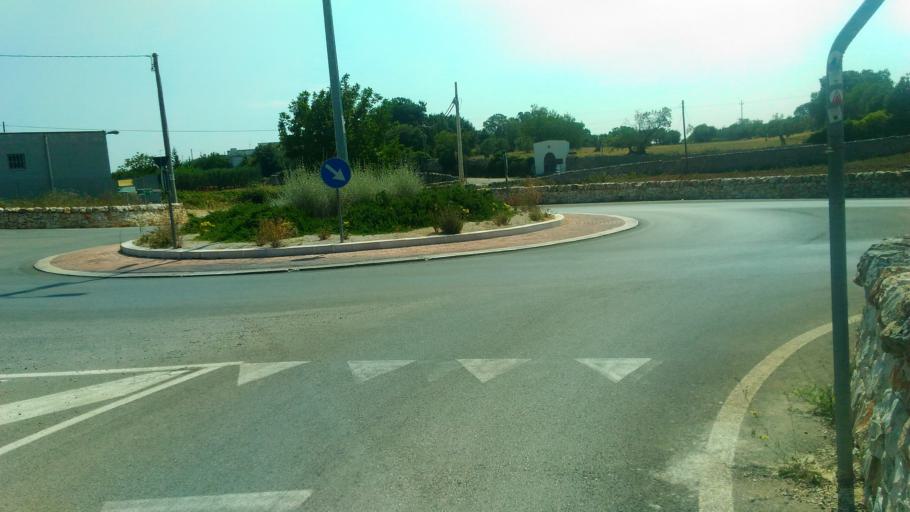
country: IT
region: Apulia
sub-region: Provincia di Bari
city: Locorotondo
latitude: 40.7519
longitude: 17.3452
